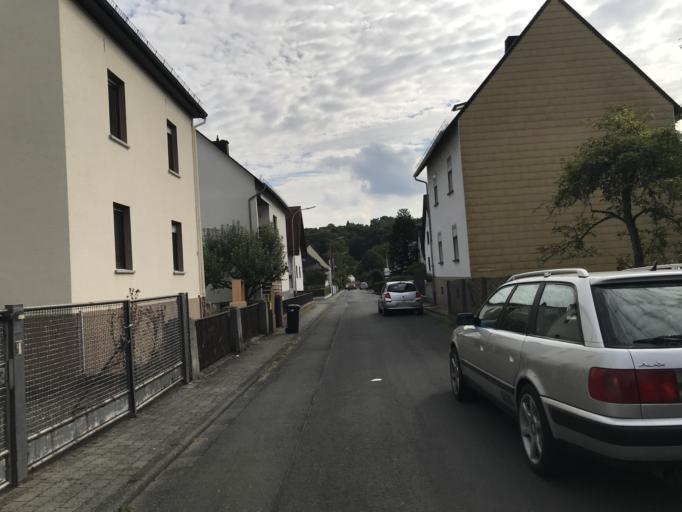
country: DE
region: Hesse
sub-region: Regierungsbezirk Giessen
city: Ehringshausen
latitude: 50.5974
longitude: 8.4147
